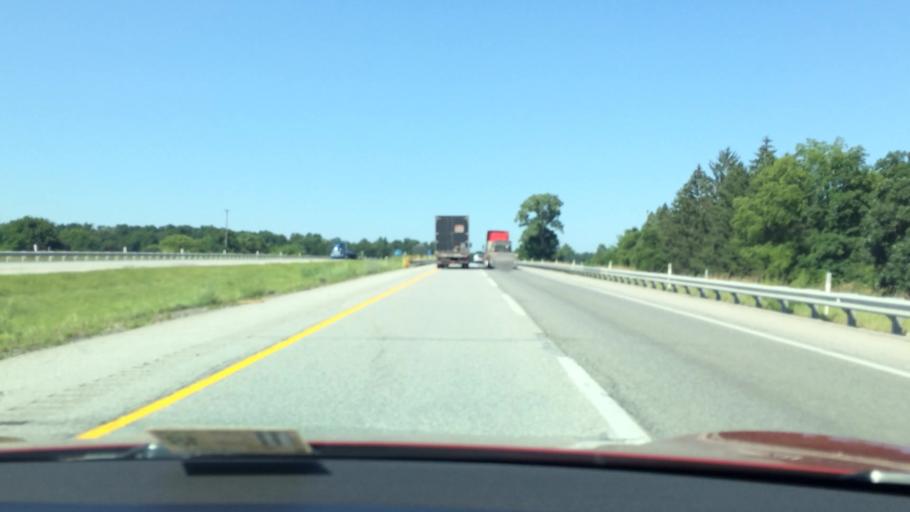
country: US
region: Indiana
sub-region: Elkhart County
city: Bristol
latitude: 41.7338
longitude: -85.8398
